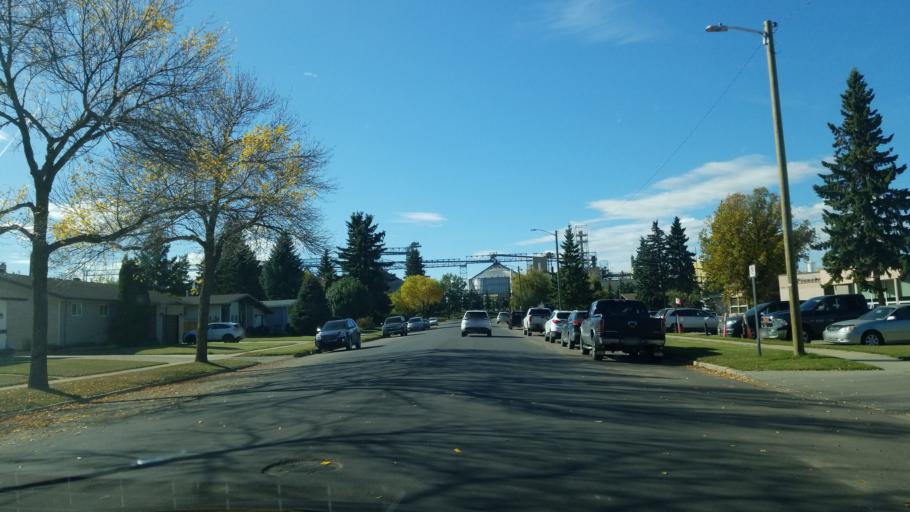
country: CA
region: Saskatchewan
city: Lloydminster
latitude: 53.2835
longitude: -110.0265
